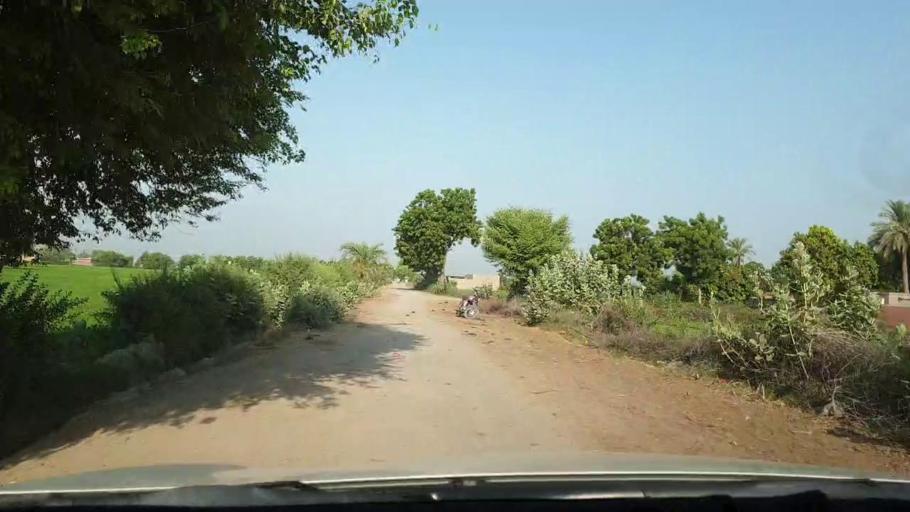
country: PK
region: Sindh
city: Larkana
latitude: 27.5451
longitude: 68.2666
